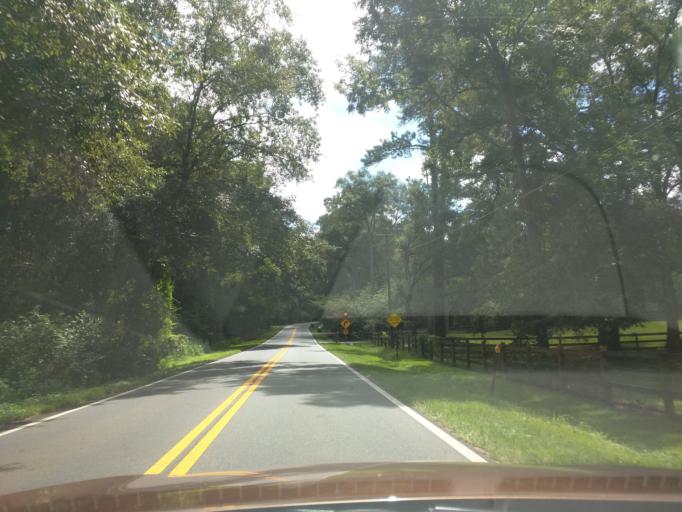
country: US
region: Florida
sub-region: Leon County
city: Tallahassee
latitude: 30.5589
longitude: -84.1805
